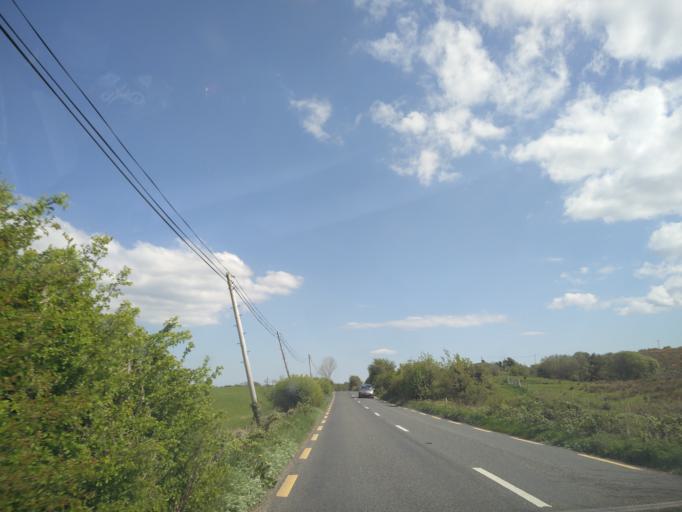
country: IE
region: Connaught
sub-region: Maigh Eo
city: Westport
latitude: 53.7851
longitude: -9.4538
